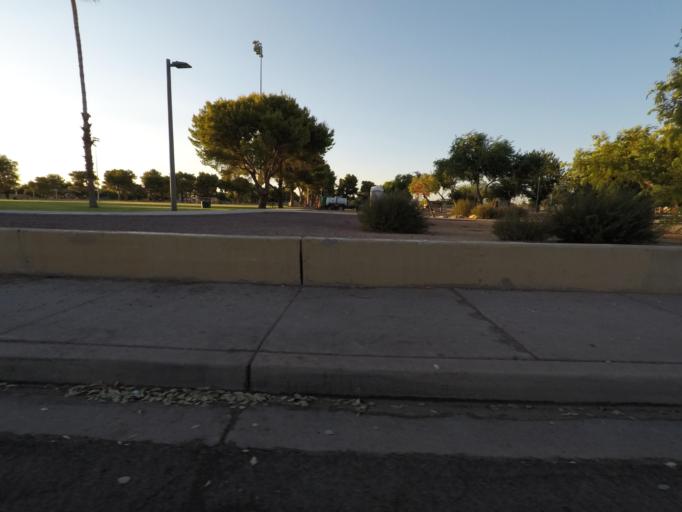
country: US
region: Arizona
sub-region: Maricopa County
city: Glendale
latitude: 33.5022
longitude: -112.1302
